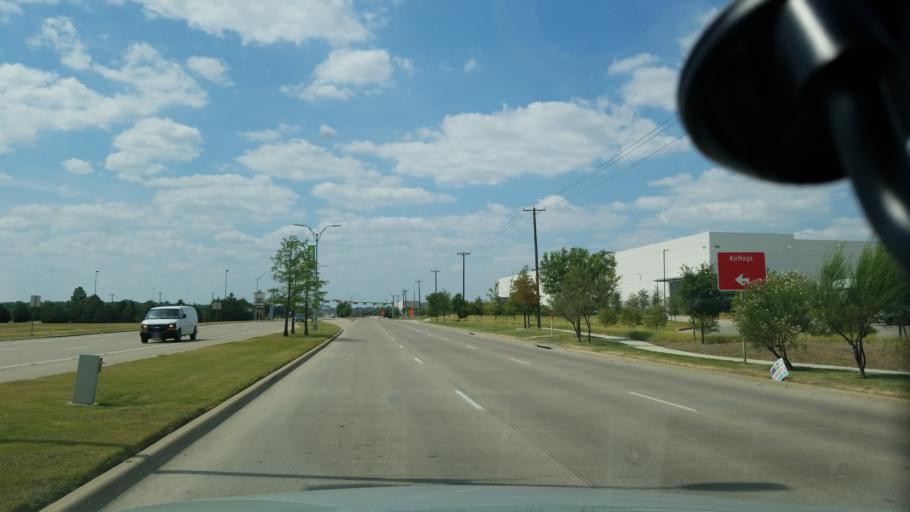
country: US
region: Texas
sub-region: Dallas County
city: Grand Prairie
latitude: 32.7723
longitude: -96.9948
